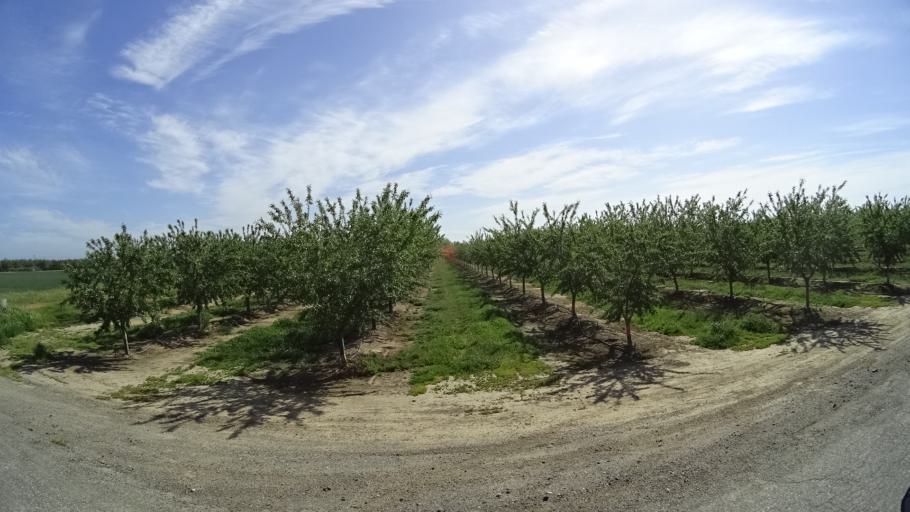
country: US
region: California
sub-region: Glenn County
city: Hamilton City
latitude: 39.6431
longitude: -122.0180
